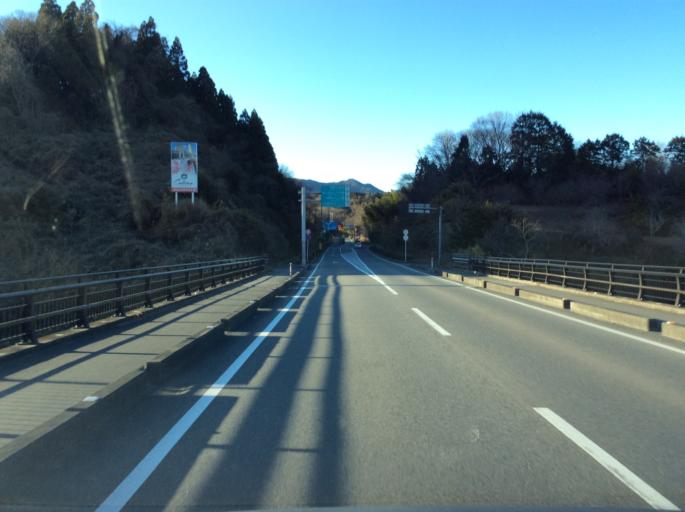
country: JP
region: Ibaraki
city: Kitaibaraki
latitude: 36.9078
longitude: 140.7487
